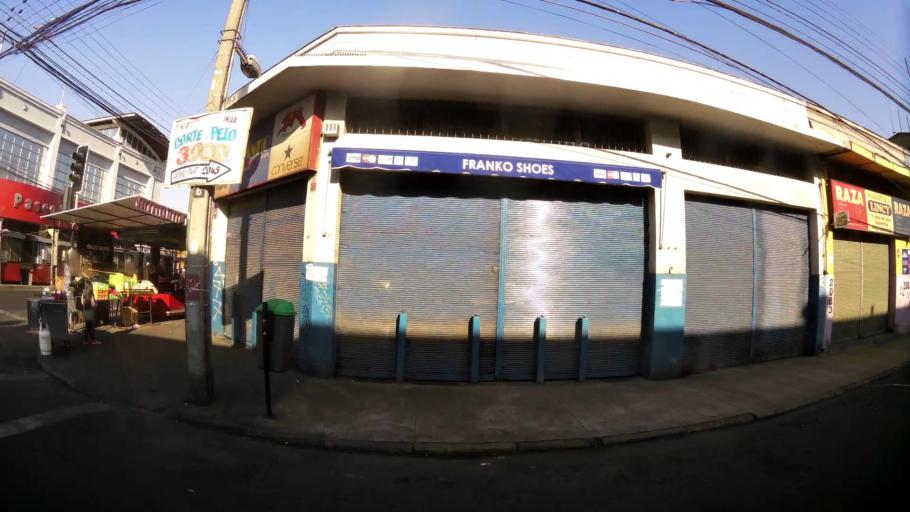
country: CL
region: Santiago Metropolitan
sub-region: Provincia de Santiago
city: Santiago
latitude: -33.4730
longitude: -70.6467
